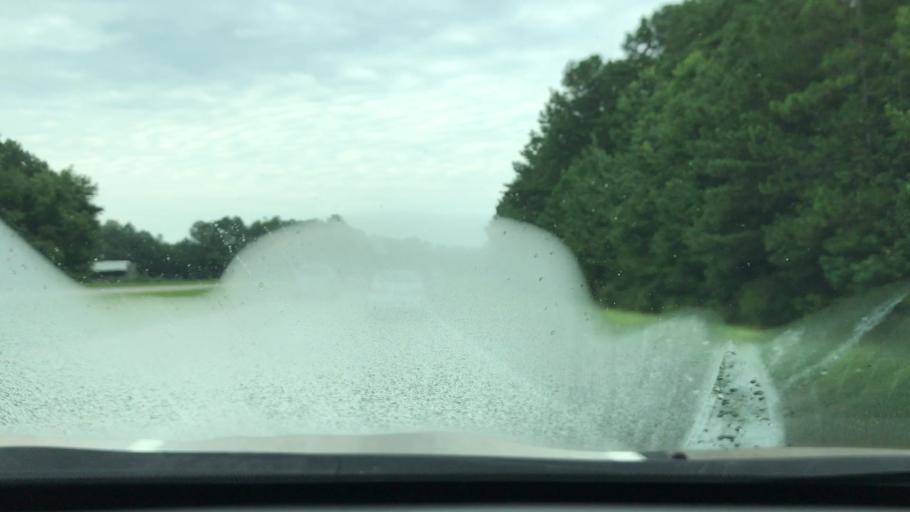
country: US
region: South Carolina
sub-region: Jasper County
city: Hardeeville
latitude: 32.2865
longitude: -81.0677
